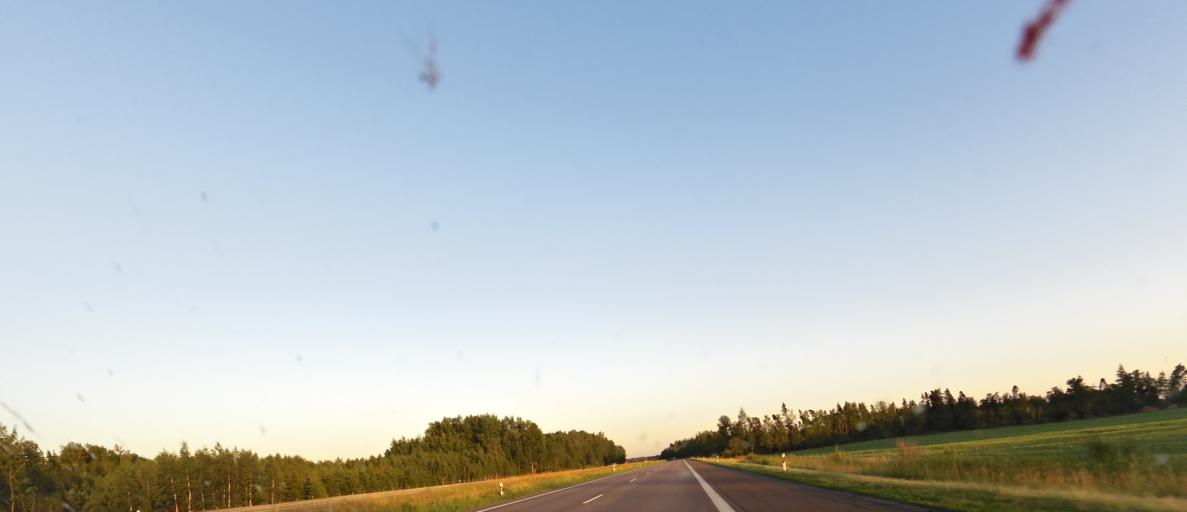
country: LT
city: Sirvintos
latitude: 55.0394
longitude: 24.8971
